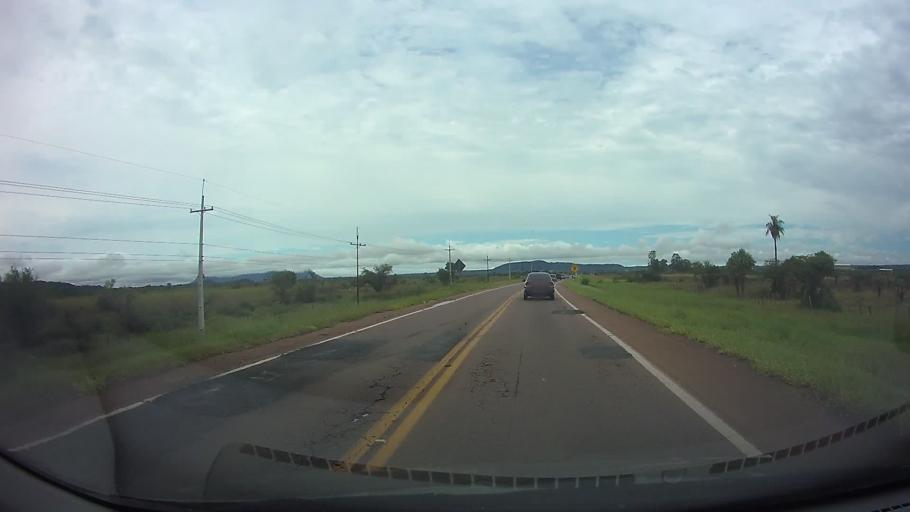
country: PY
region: Paraguari
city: Carapegua
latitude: -25.7281
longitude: -57.2057
